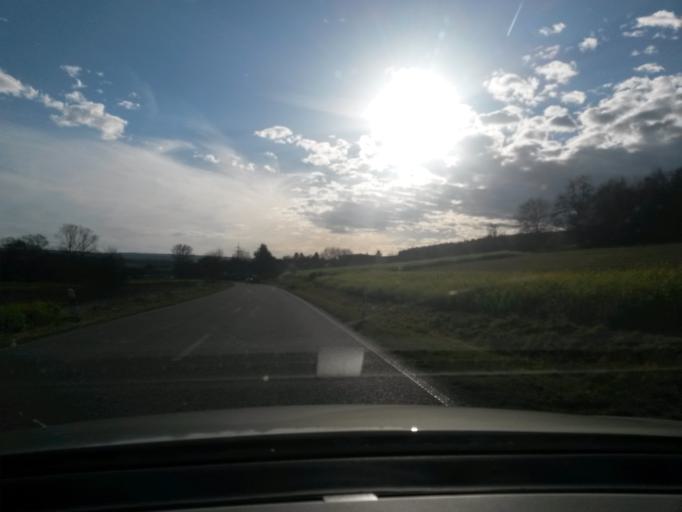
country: DE
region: Baden-Wuerttemberg
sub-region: Karlsruhe Region
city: Konigsbach-Stein
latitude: 48.9190
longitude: 8.5604
